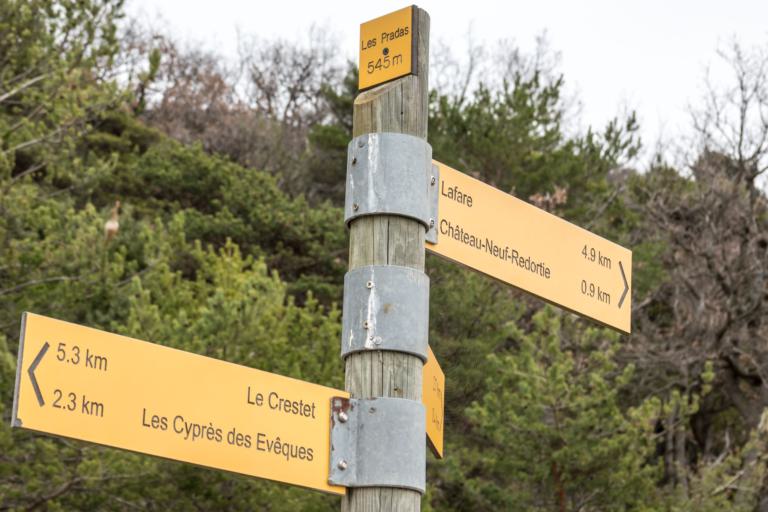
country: FR
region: Provence-Alpes-Cote d'Azur
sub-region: Departement du Vaucluse
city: Sablet
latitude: 44.1797
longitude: 5.0546
